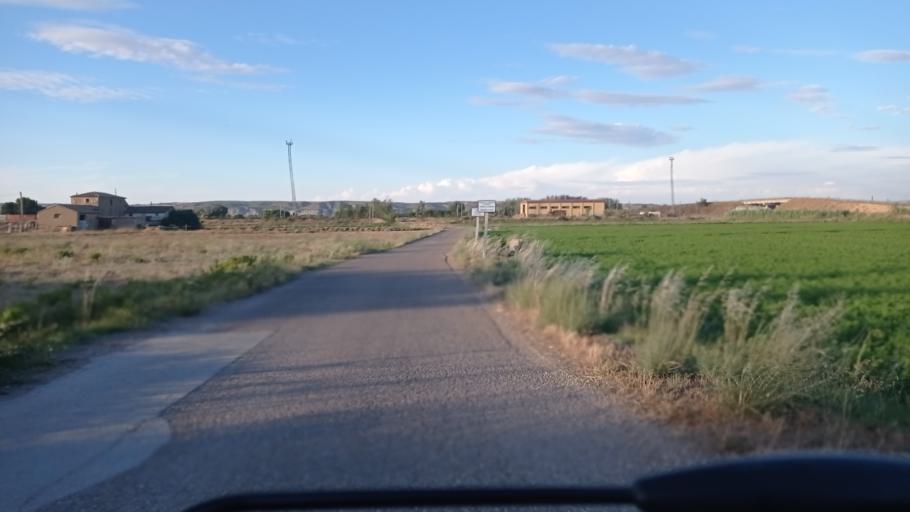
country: ES
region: Aragon
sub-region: Provincia de Zaragoza
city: Oliver-Valdefierro, Oliver, Valdefierro
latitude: 41.6741
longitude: -0.9450
